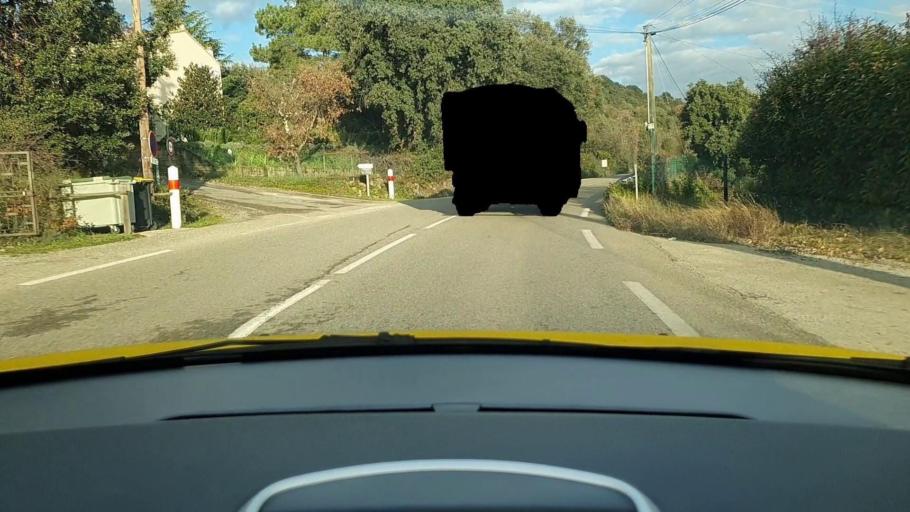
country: FR
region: Languedoc-Roussillon
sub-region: Departement du Gard
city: Laval-Pradel
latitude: 44.1923
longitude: 4.0838
